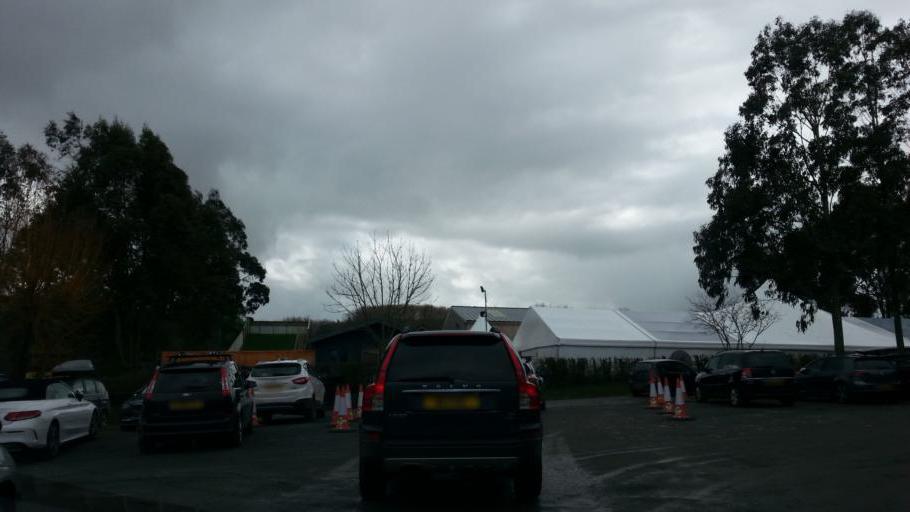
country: GB
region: England
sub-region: Devon
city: Northam
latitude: 51.0165
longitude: -4.2446
